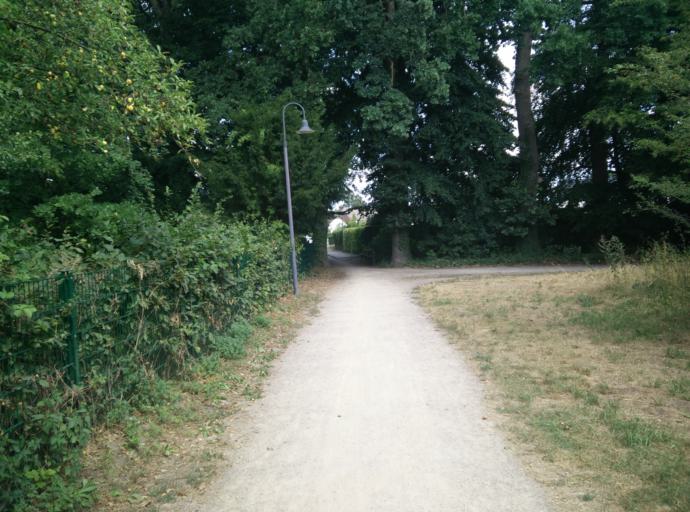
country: DE
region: North Rhine-Westphalia
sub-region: Regierungsbezirk Arnsberg
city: Lippstadt
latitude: 51.6891
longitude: 8.3580
